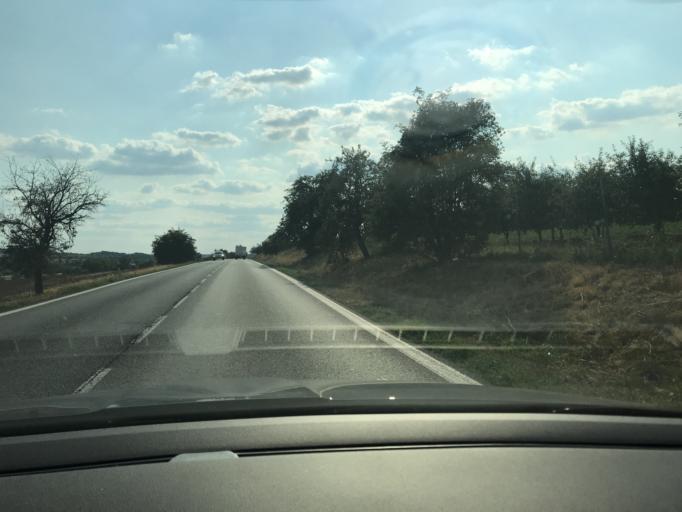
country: CZ
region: Central Bohemia
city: Brandysek
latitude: 50.2574
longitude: 14.1673
